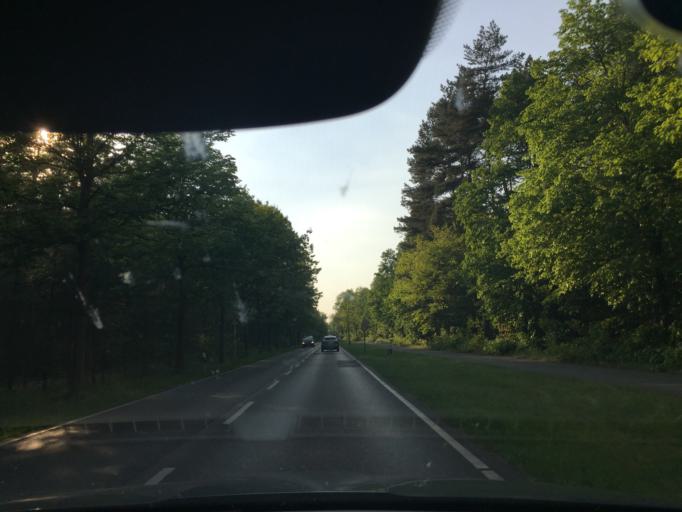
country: DE
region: Berlin
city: Grunau
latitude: 52.4016
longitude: 13.5980
